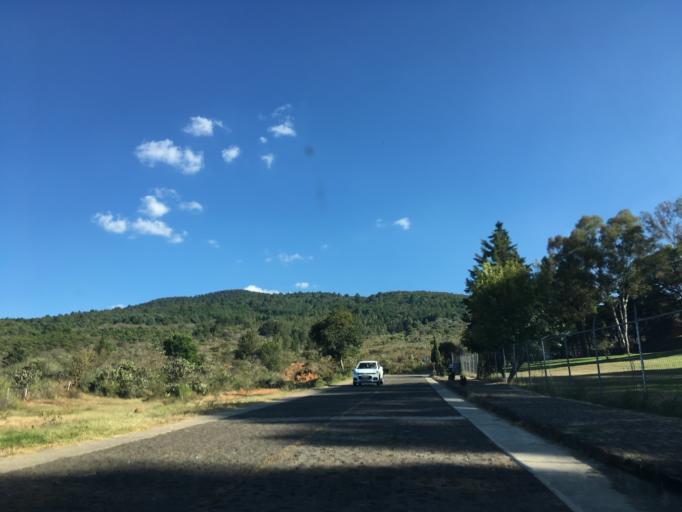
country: MX
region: Michoacan
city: Tzintzuntzan
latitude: 19.6256
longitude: -101.5721
